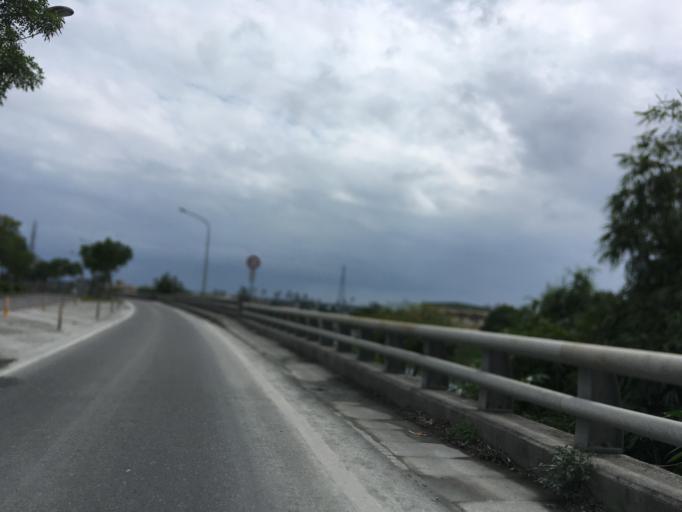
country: TW
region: Taiwan
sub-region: Yilan
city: Yilan
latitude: 24.6775
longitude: 121.7830
